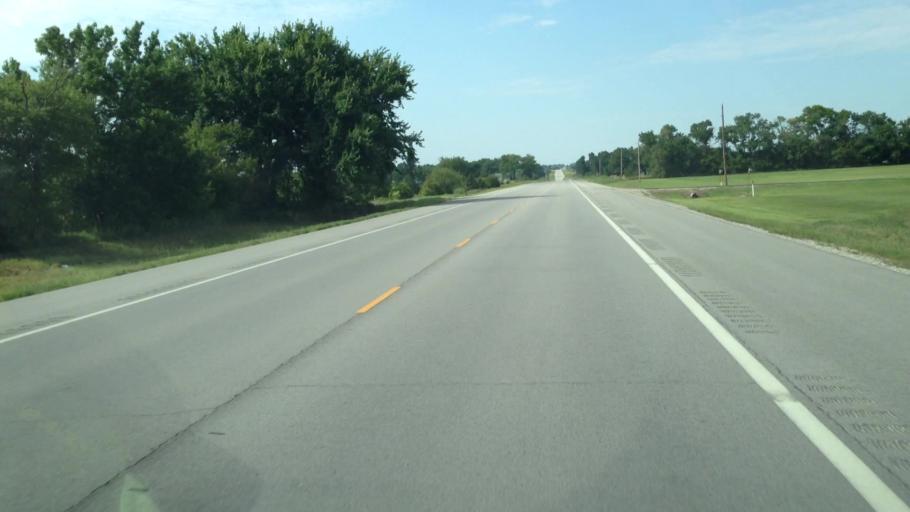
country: US
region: Kansas
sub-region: Labette County
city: Altamont
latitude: 37.2605
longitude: -95.2672
